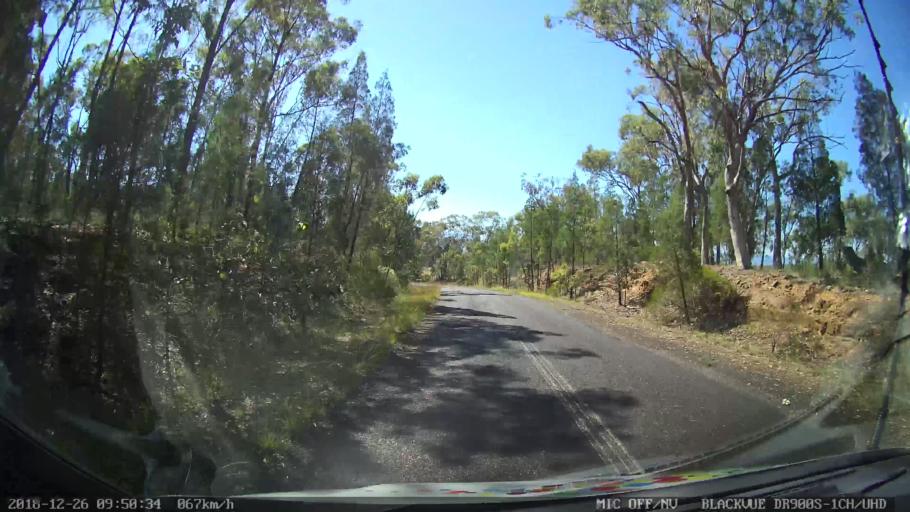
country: AU
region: New South Wales
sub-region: Mid-Western Regional
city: Kandos
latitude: -32.9981
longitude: 150.1349
